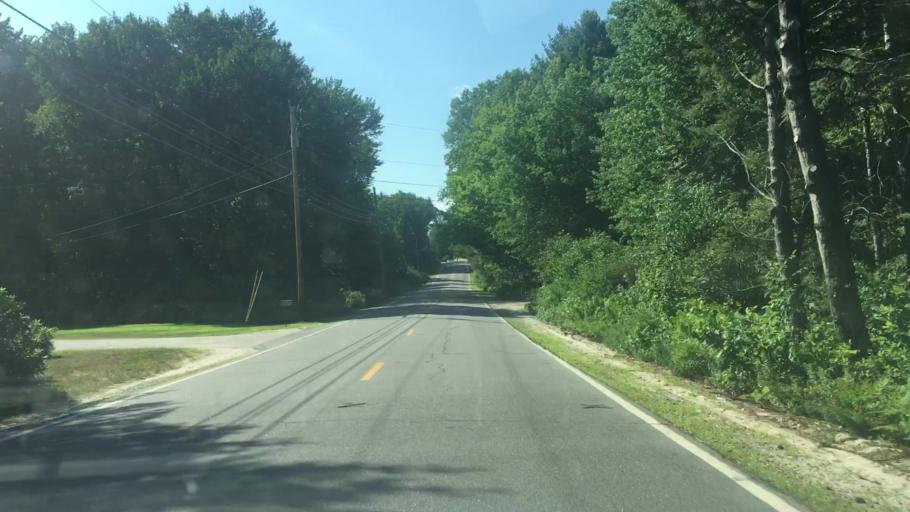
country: US
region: Maine
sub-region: York County
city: Hollis Center
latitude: 43.6387
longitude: -70.5799
